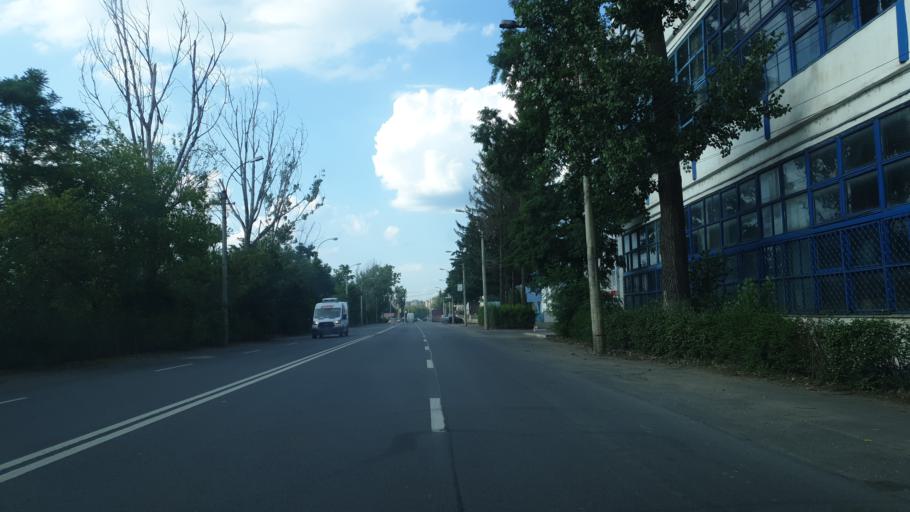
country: RO
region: Covasna
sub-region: Municipiul Sfantu Gheorghe
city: Sfantu-Gheorghe
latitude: 45.8484
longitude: 25.8054
